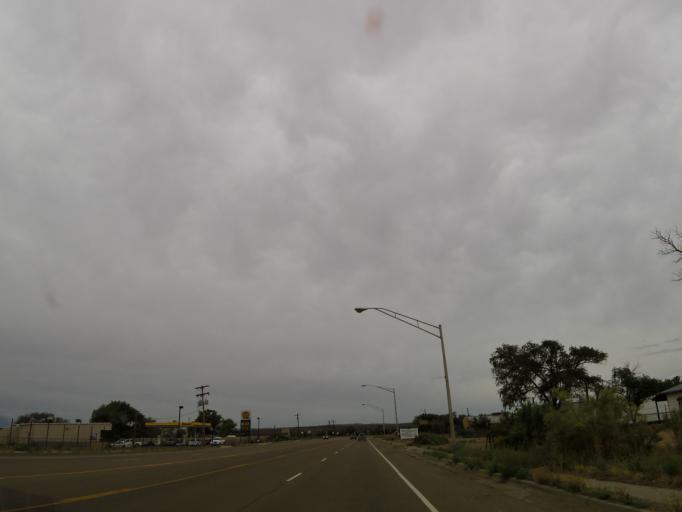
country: US
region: New Mexico
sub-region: Sandoval County
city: Jemez Pueblo
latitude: 35.5517
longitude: -106.7785
